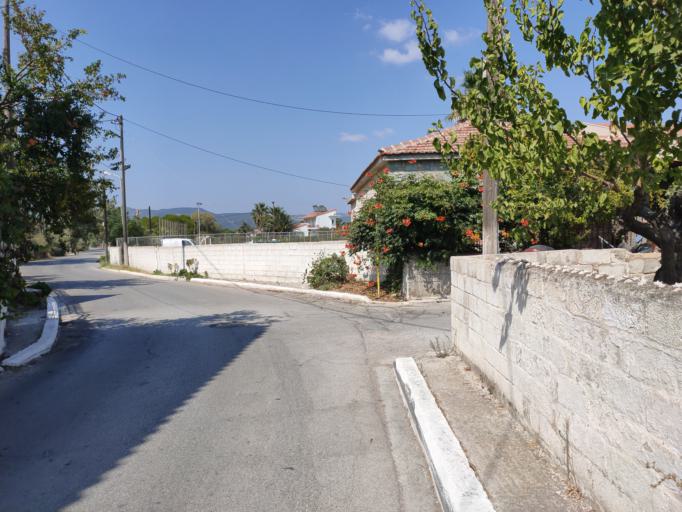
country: GR
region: North Aegean
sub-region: Nomos Lesvou
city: Kalloni
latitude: 39.2068
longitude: 26.2093
